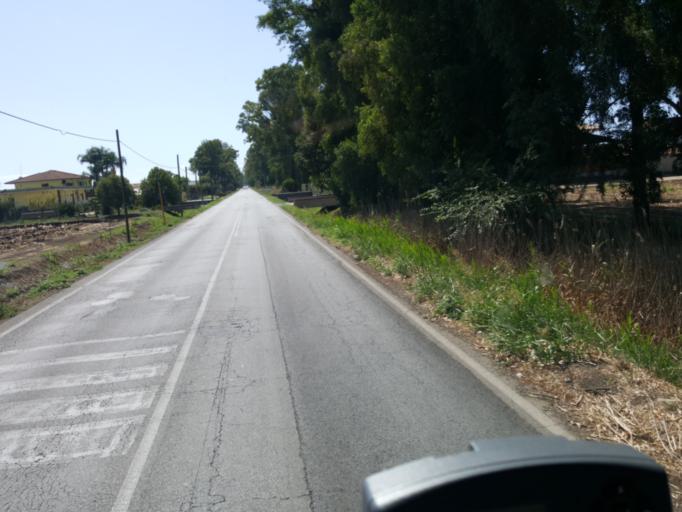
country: IT
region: Latium
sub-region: Provincia di Latina
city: Borgo Hermada
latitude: 41.3648
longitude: 13.1162
